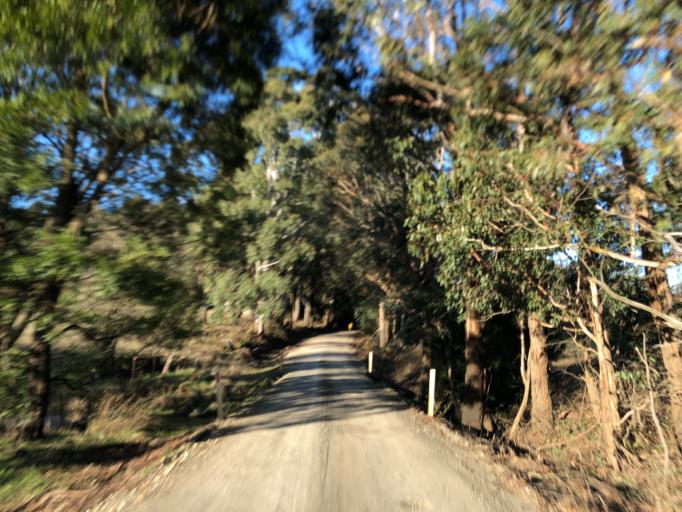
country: AU
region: Victoria
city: Brown Hill
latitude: -37.4796
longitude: 144.1542
